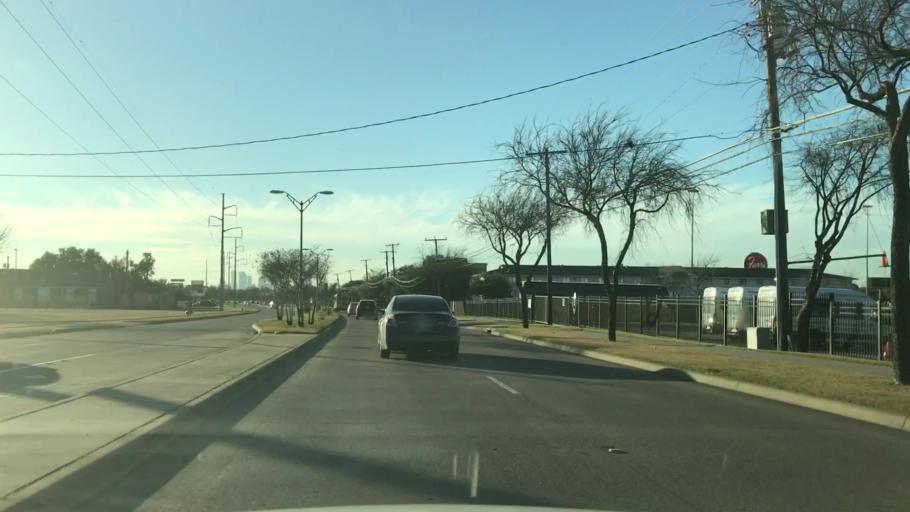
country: US
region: Texas
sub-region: Dallas County
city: Balch Springs
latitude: 32.7927
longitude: -96.6939
